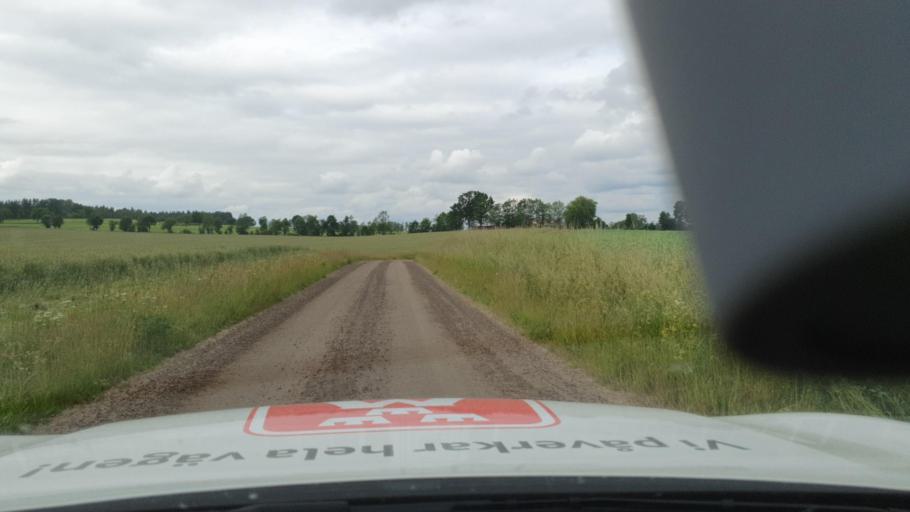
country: SE
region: Vaestra Goetaland
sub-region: Hjo Kommun
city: Hjo
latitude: 58.1914
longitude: 14.1752
